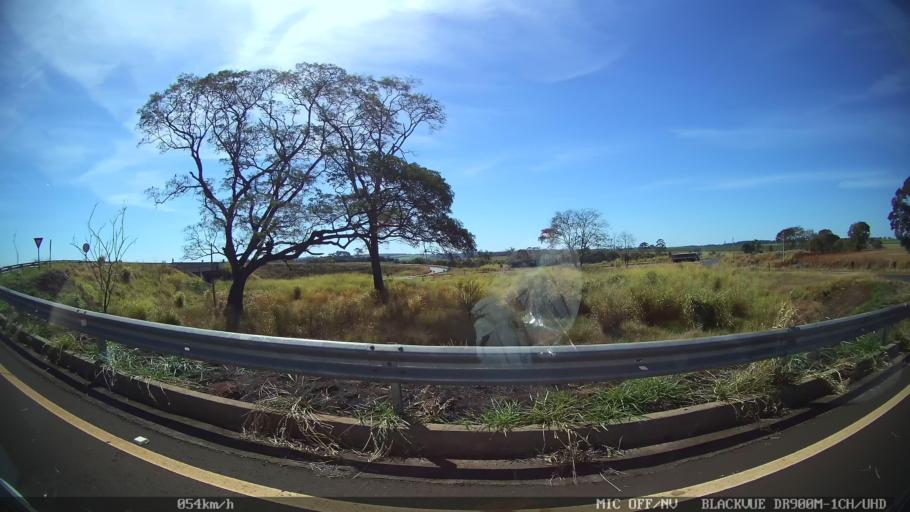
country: BR
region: Sao Paulo
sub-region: Nuporanga
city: Nuporanga
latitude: -20.5623
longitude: -47.6246
